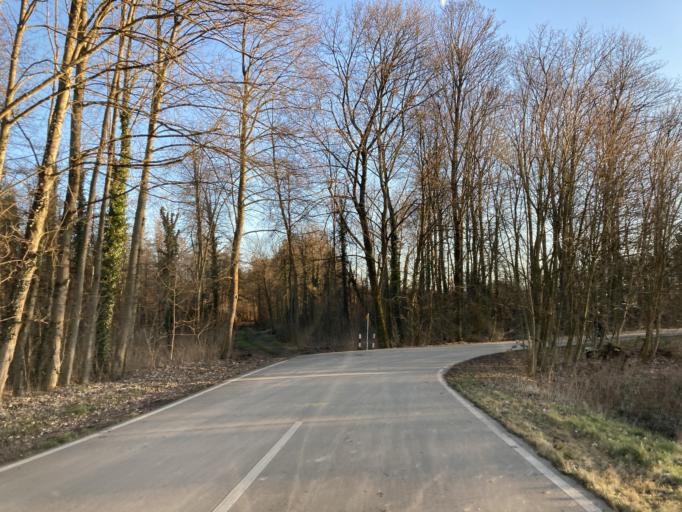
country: DE
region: Baden-Wuerttemberg
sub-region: Freiburg Region
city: Umkirch
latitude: 48.0511
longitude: 7.7693
